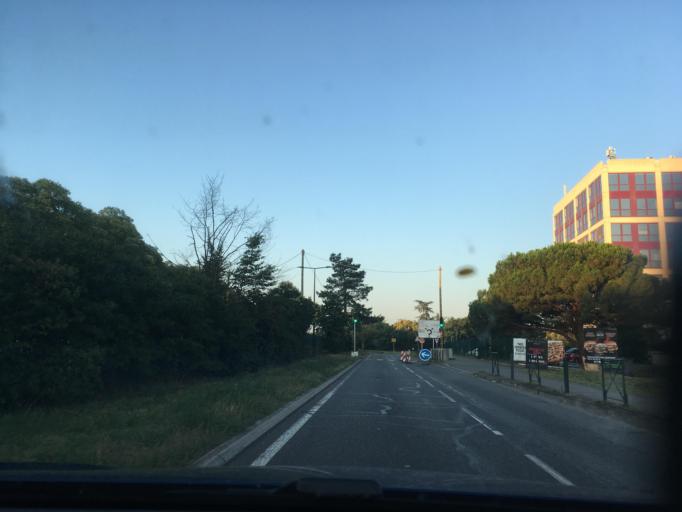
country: FR
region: Midi-Pyrenees
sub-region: Departement de la Haute-Garonne
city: Blagnac
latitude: 43.5798
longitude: 1.3953
